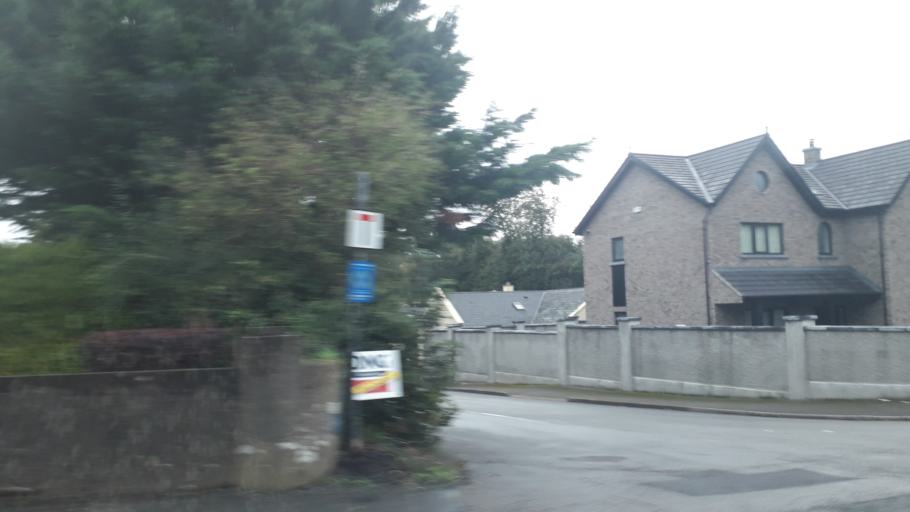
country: IE
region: Leinster
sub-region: An Longfort
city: Longford
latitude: 53.7359
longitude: -7.8005
